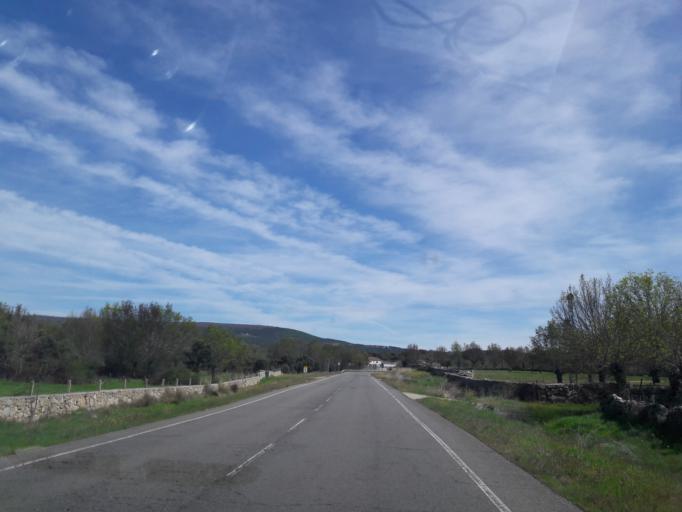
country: ES
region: Castille and Leon
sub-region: Provincia de Salamanca
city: Ledrada
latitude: 40.4875
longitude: -5.7225
